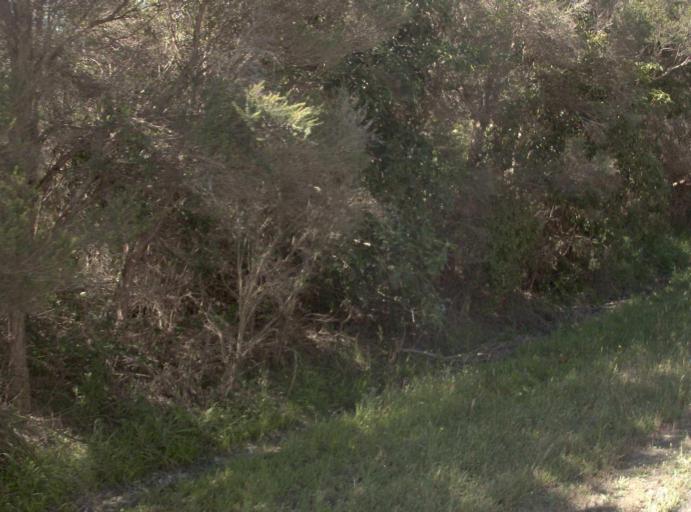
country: AU
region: Victoria
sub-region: Latrobe
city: Morwell
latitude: -38.6667
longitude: 146.4063
